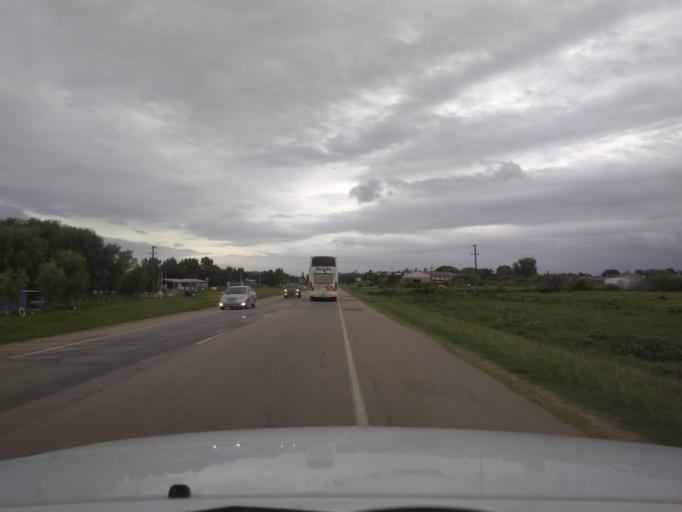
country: UY
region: Canelones
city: Canelones
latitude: -34.5105
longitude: -56.2786
